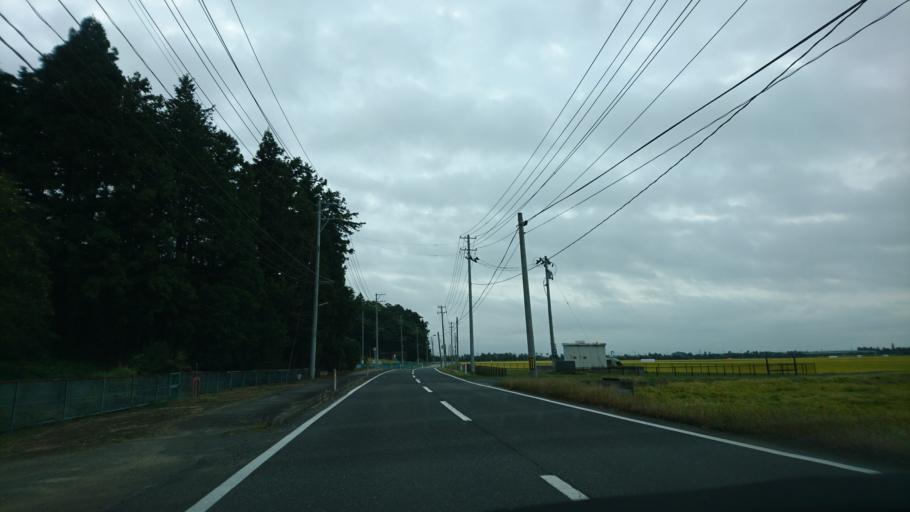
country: JP
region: Iwate
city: Ichinoseki
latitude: 38.8071
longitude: 141.0860
